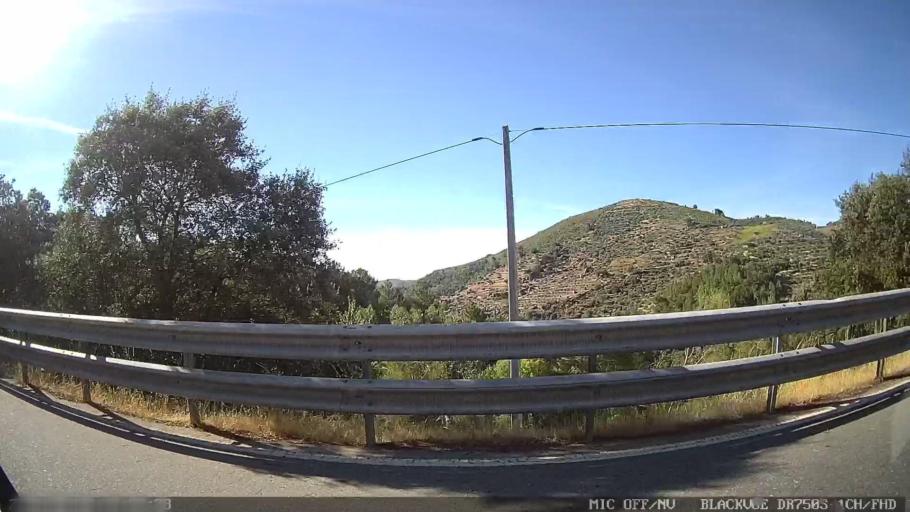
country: PT
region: Vila Real
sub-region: Murca
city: Murca
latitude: 41.4081
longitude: -7.4704
